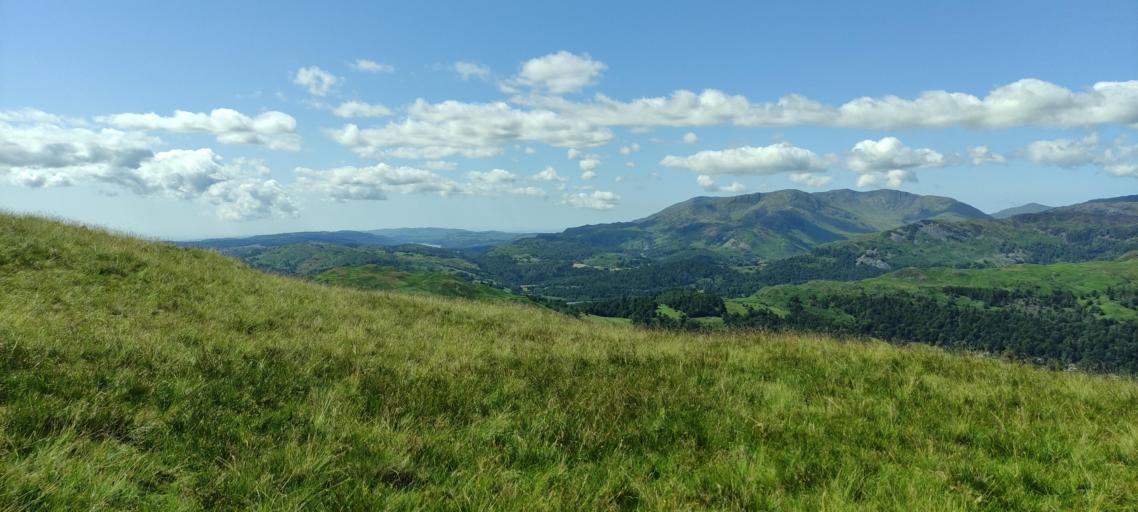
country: GB
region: England
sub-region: Cumbria
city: Ambleside
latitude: 54.4587
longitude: -2.9971
